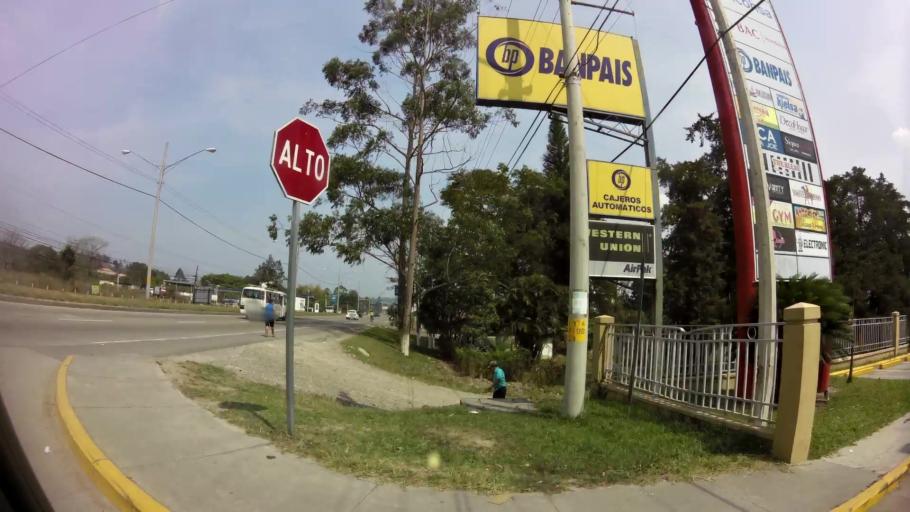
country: HN
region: Comayagua
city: Siguatepeque
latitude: 14.5836
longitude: -87.8466
